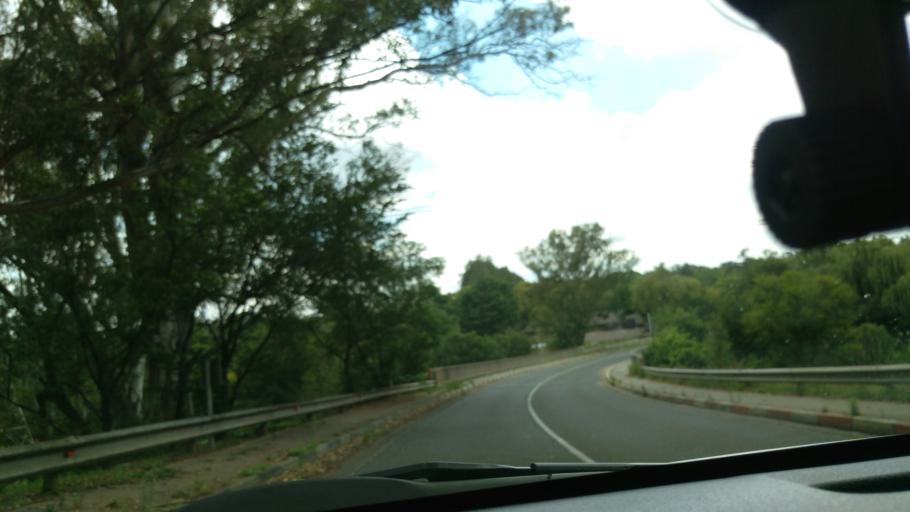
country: ZA
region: Gauteng
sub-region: City of Johannesburg Metropolitan Municipality
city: Midrand
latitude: -26.0427
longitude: 28.0498
